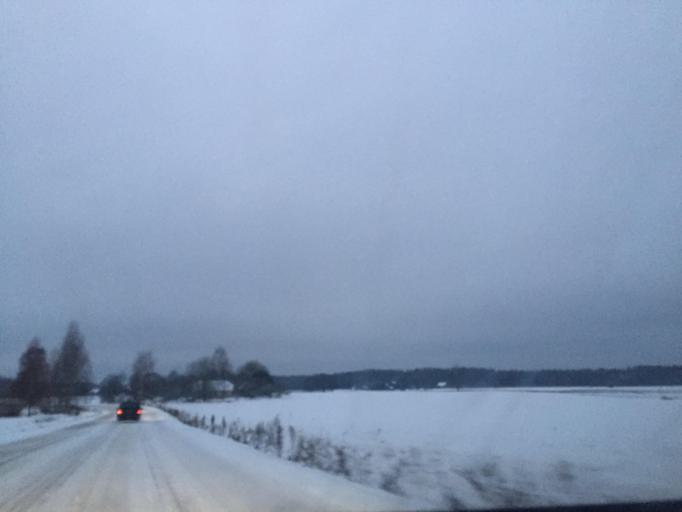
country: LV
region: Raunas
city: Rauna
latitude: 57.4187
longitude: 25.5601
